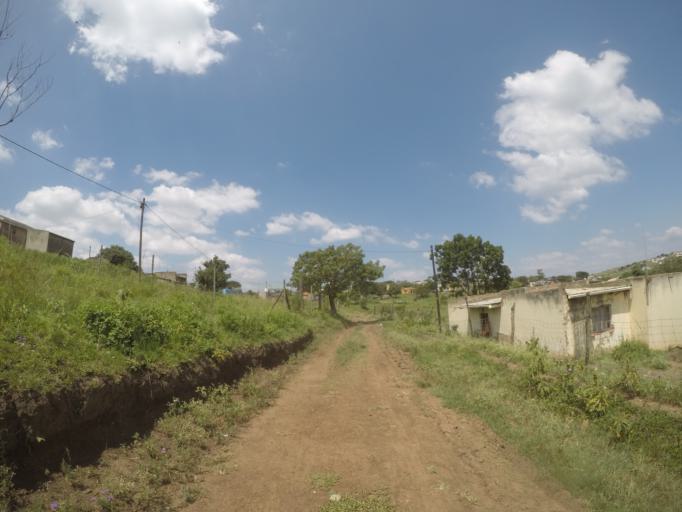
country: ZA
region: KwaZulu-Natal
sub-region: uThungulu District Municipality
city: Empangeni
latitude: -28.6010
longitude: 31.7398
